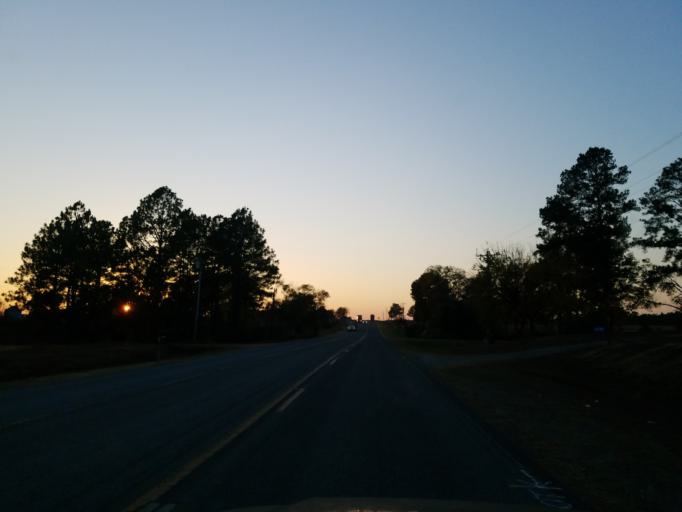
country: US
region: Georgia
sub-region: Ben Hill County
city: Fitzgerald
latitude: 31.7201
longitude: -83.4042
